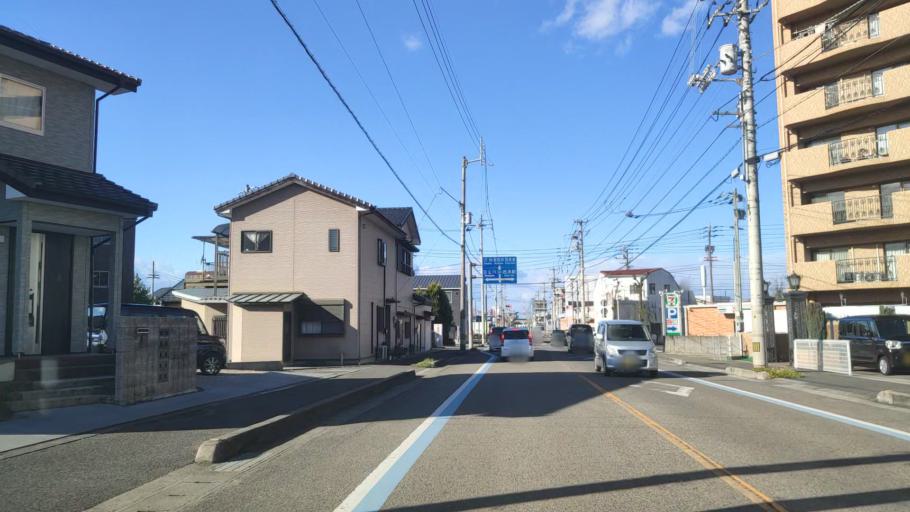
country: JP
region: Ehime
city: Saijo
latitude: 33.9109
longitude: 133.1808
